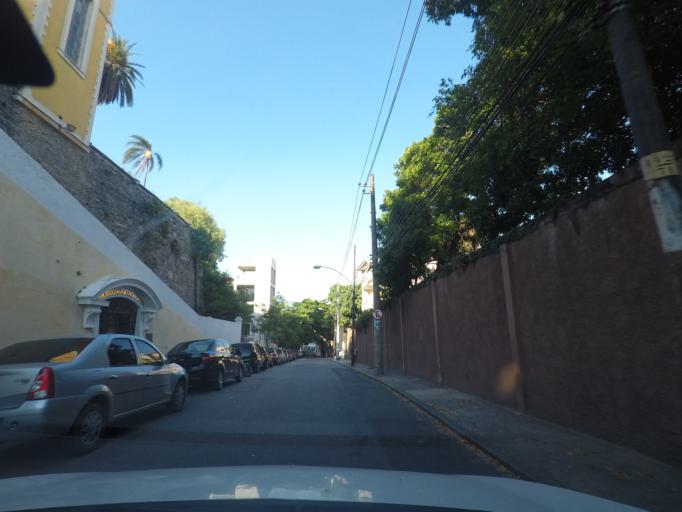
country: BR
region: Rio de Janeiro
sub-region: Rio De Janeiro
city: Rio de Janeiro
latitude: -22.8960
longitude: -43.2228
